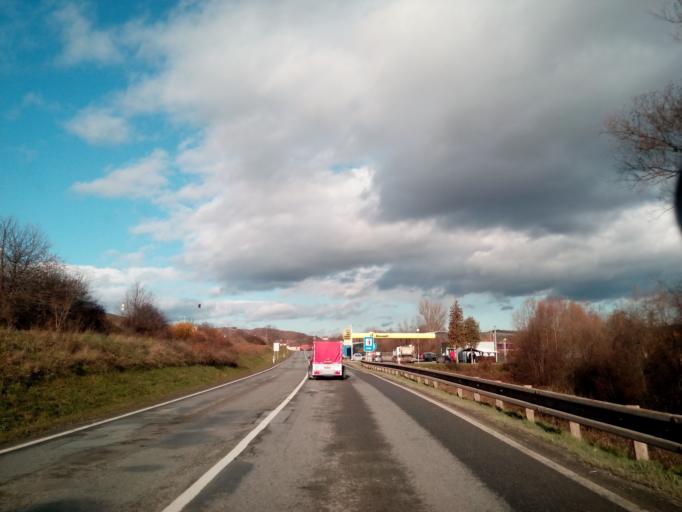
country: SK
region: Presovsky
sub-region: Okres Bardejov
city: Bardejov
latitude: 49.1423
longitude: 21.3234
